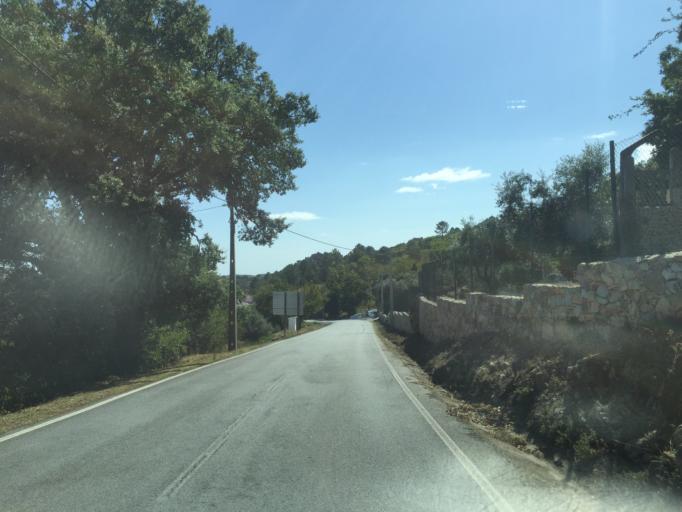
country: PT
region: Portalegre
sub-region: Marvao
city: Marvao
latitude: 39.4027
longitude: -7.3797
